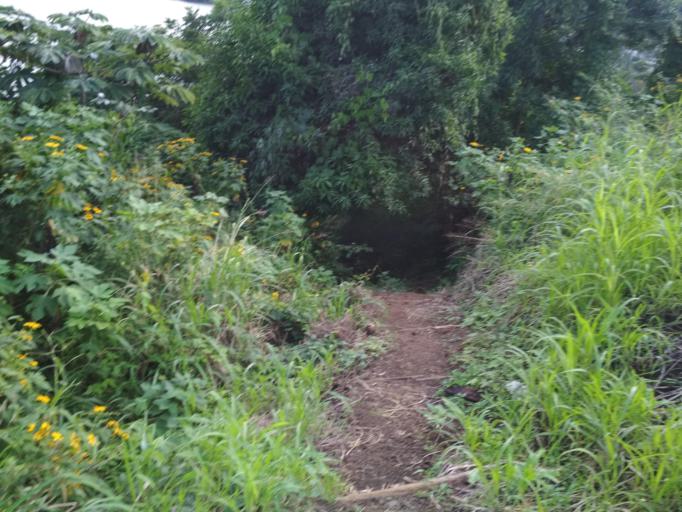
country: MX
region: Veracruz
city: Catemaco
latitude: 18.3923
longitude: -95.1218
